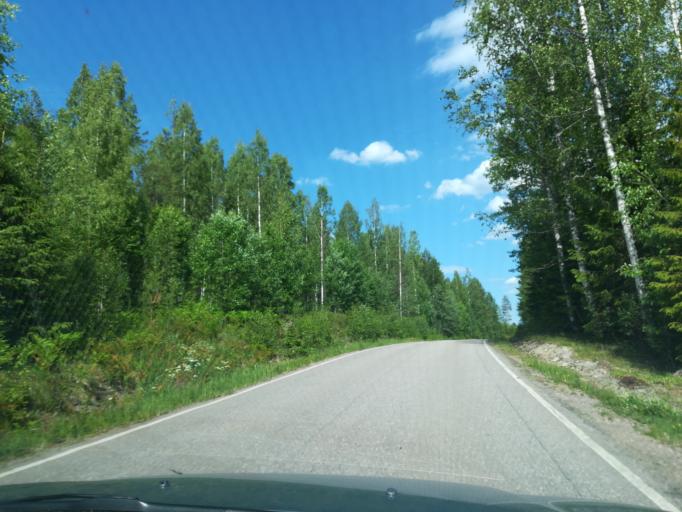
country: FI
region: South Karelia
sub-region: Imatra
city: Ruokolahti
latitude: 61.4721
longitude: 28.8354
